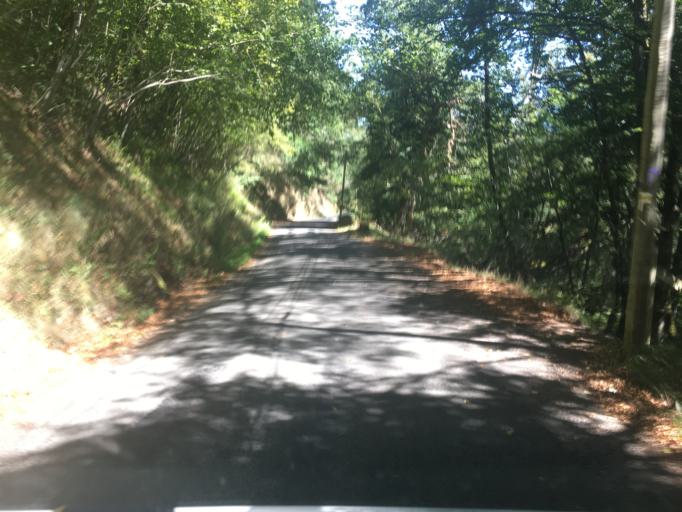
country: FR
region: Limousin
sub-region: Departement de la Correze
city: Bort-les-Orgues
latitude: 45.3928
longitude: 2.4862
